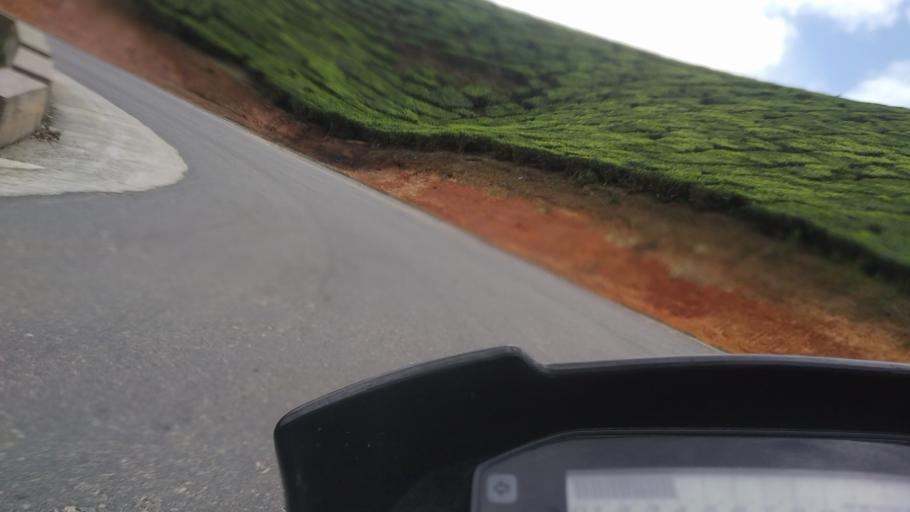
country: IN
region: Kerala
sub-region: Idukki
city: Munnar
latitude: 10.0467
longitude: 77.1127
